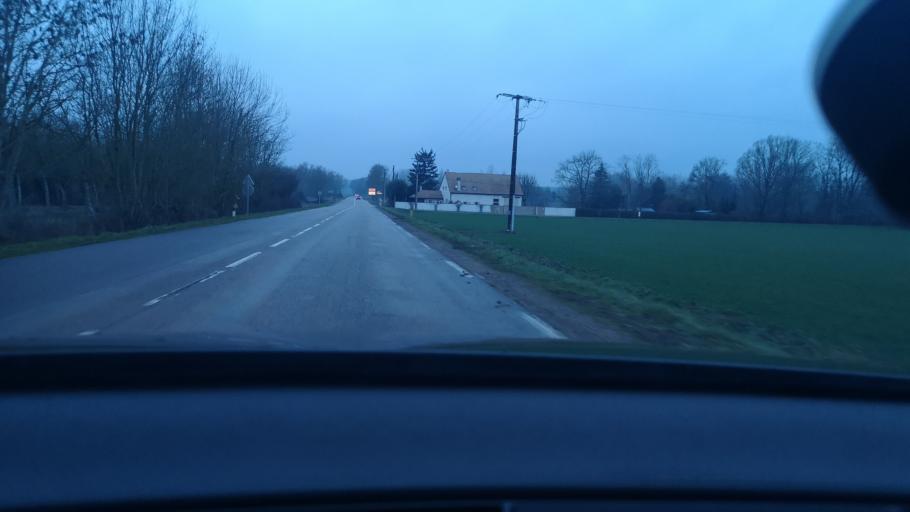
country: FR
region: Bourgogne
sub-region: Departement de Saone-et-Loire
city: Verdun-sur-le-Doubs
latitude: 47.0082
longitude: 4.9909
